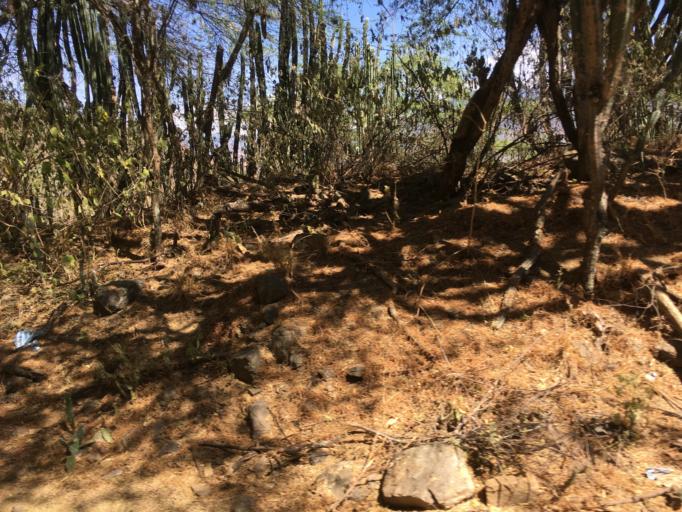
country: CO
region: Santander
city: Aratoca
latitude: 6.7744
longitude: -72.9946
